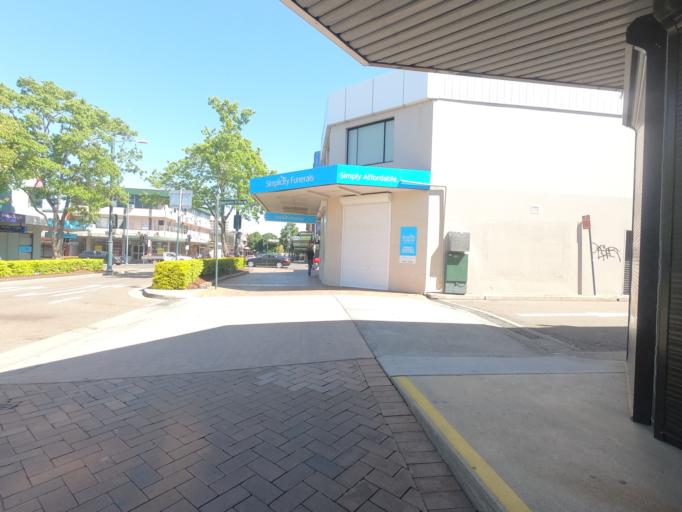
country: AU
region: New South Wales
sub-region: Fairfield
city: Liverpool
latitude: -33.9220
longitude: 150.9225
